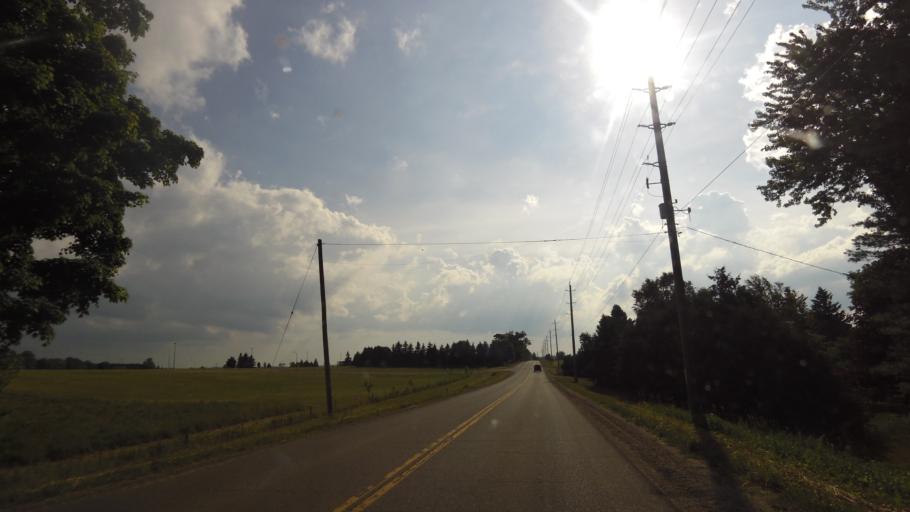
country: CA
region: Ontario
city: Orangeville
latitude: 43.9525
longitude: -80.0719
